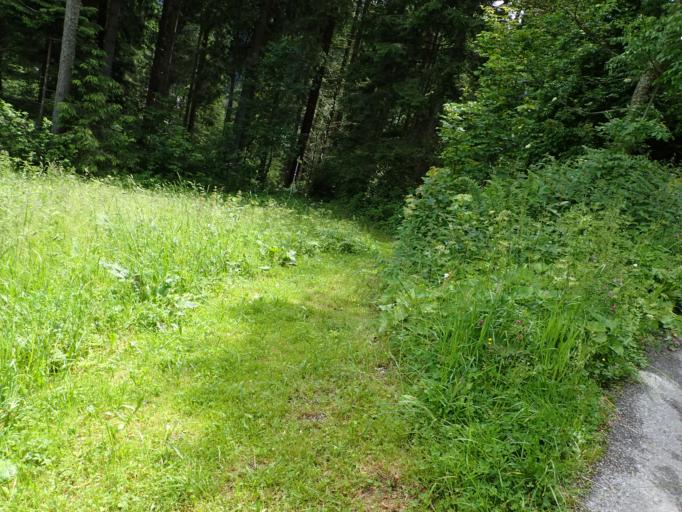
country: AT
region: Salzburg
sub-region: Politischer Bezirk Sankt Johann im Pongau
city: Wagrain
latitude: 47.3383
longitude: 13.3014
